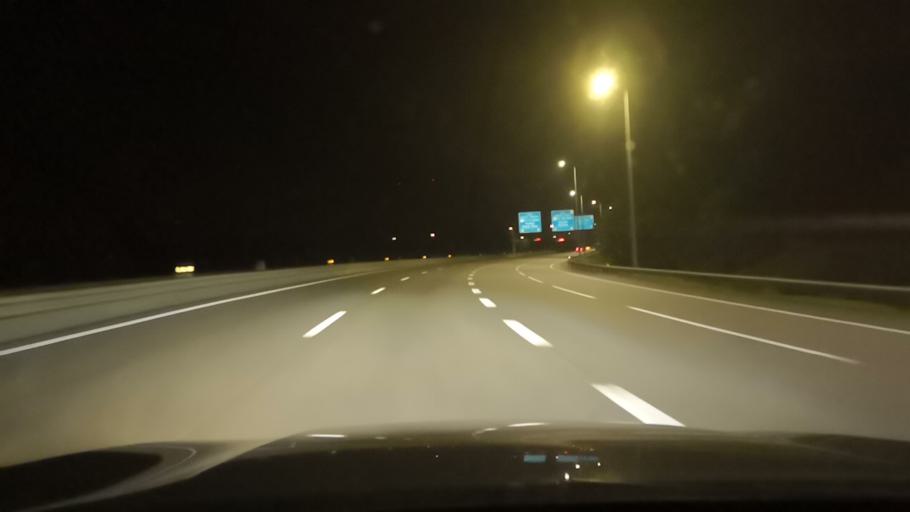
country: PT
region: Setubal
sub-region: Palmela
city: Palmela
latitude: 38.5758
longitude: -8.8662
